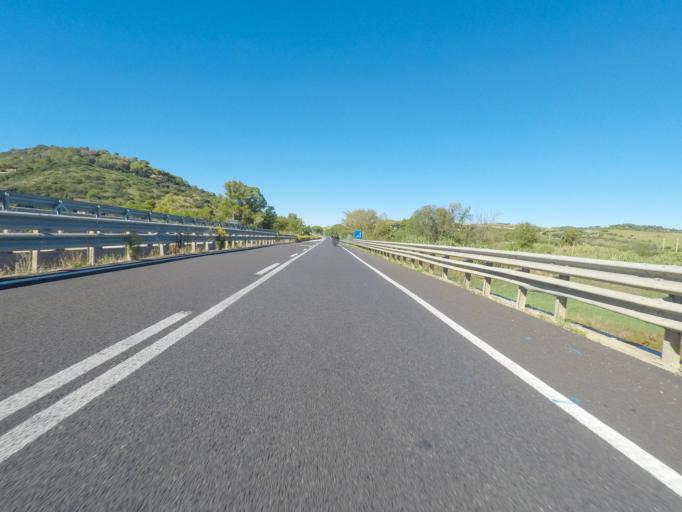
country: IT
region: Tuscany
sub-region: Provincia di Grosseto
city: Fonteblanda
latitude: 42.5486
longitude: 11.1747
